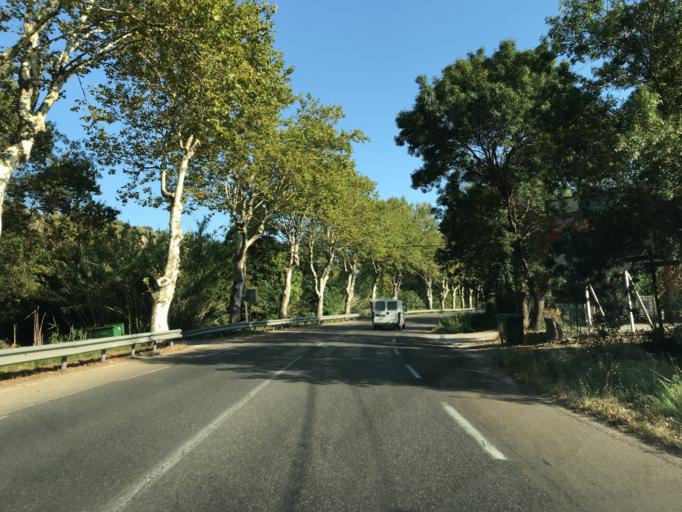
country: FR
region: Provence-Alpes-Cote d'Azur
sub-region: Departement des Bouches-du-Rhone
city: Saint-Chamas
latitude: 43.5681
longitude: 5.0238
